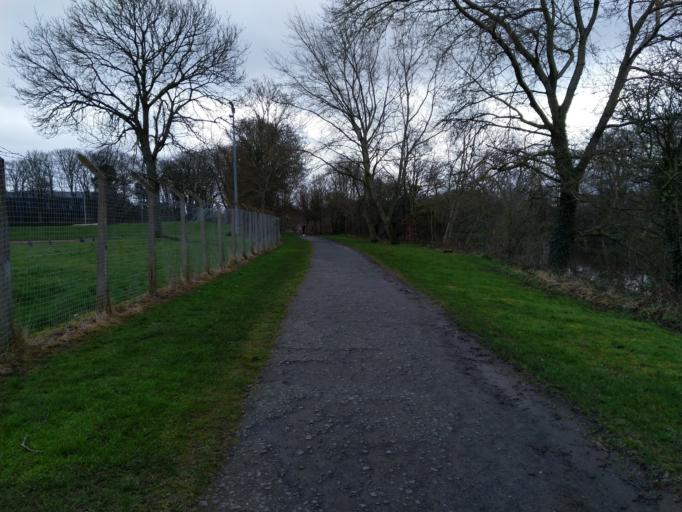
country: GB
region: Scotland
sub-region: South Ayrshire
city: Ayr
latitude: 55.4581
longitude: -4.6201
